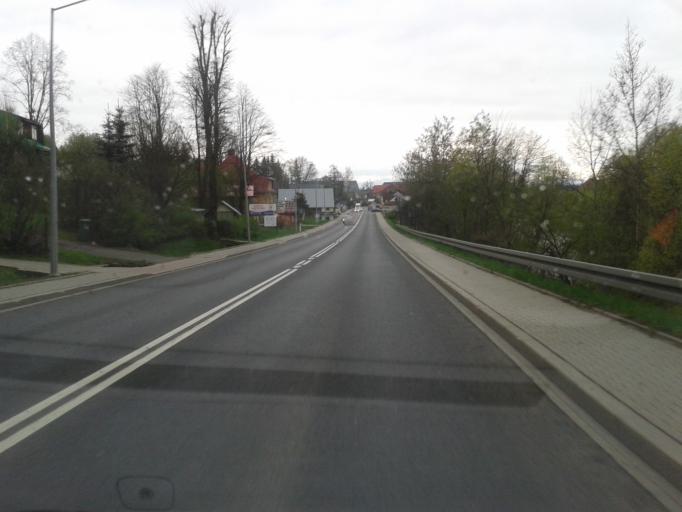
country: PL
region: Lesser Poland Voivodeship
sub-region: Powiat nowotarski
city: Jablonka
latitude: 49.4847
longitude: 19.6983
